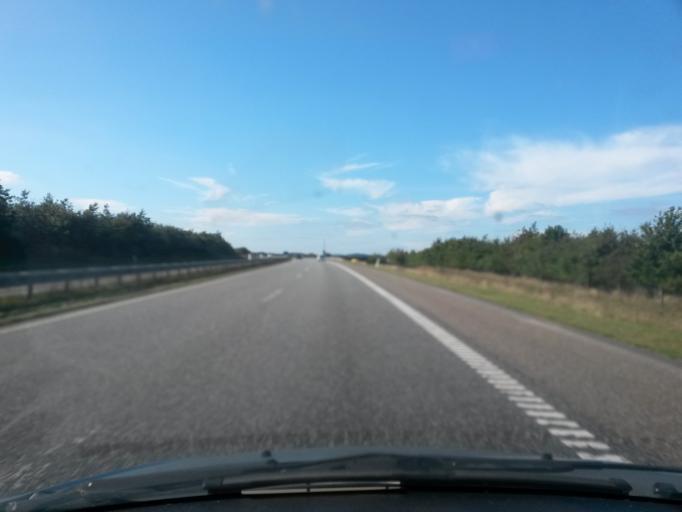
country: DK
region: Central Jutland
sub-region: Skanderborg Kommune
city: Galten
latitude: 56.1475
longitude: 9.8420
